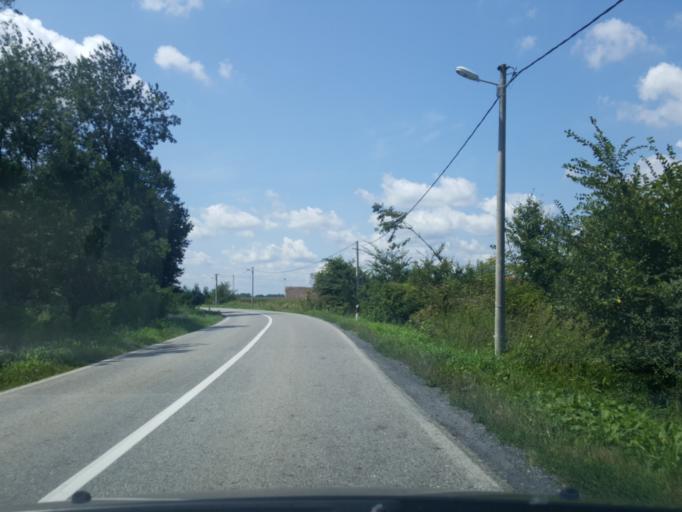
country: RS
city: Metkovic
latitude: 44.8507
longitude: 19.5281
